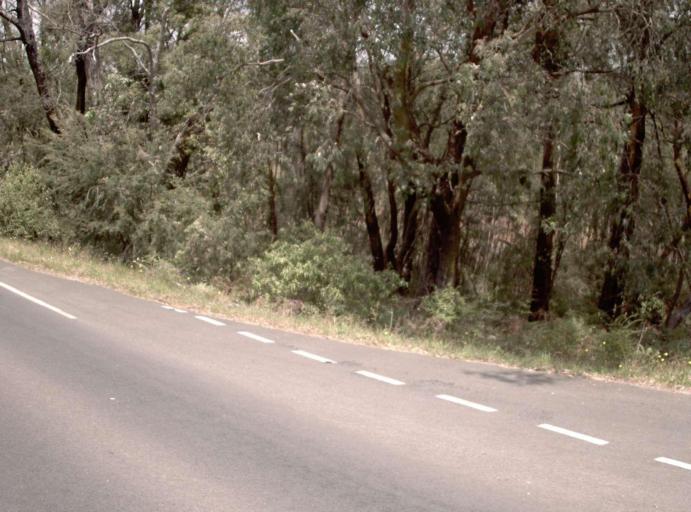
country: AU
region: Victoria
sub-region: Latrobe
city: Traralgon
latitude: -38.2826
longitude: 146.6946
